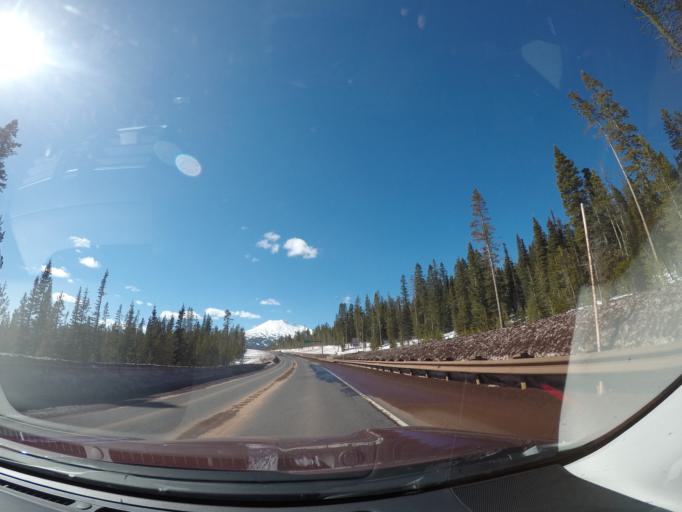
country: US
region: Oregon
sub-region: Deschutes County
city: Sunriver
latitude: 43.9839
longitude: -121.6027
